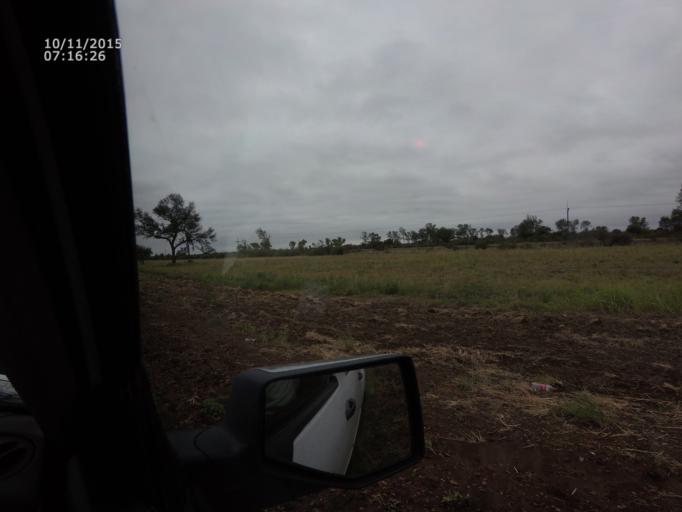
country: AR
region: Chaco
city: Pampa del Infierno
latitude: -26.4706
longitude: -61.2691
